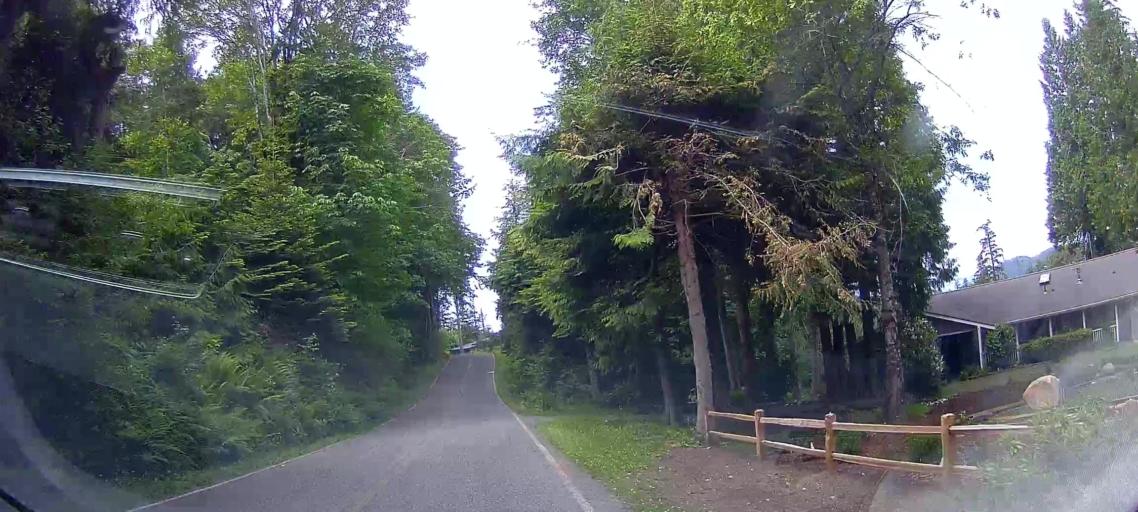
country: US
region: Washington
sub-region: Whatcom County
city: Bellingham
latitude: 48.6620
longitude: -122.4942
